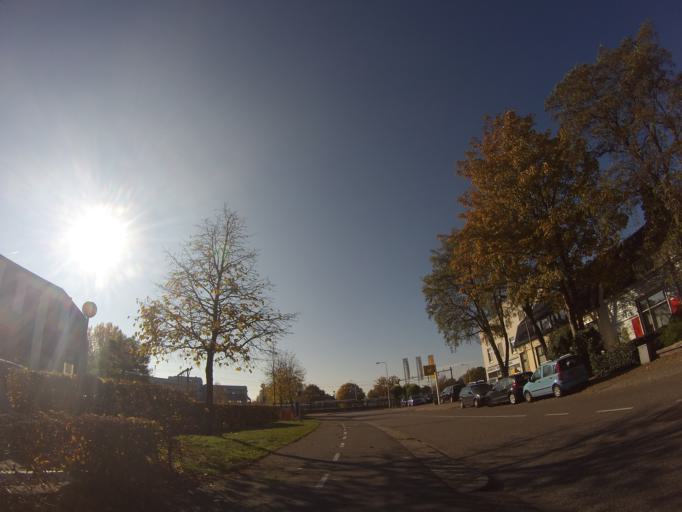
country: NL
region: Utrecht
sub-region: Gemeente Utrechtse Heuvelrug
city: Driebergen-Rijsenburg
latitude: 52.0660
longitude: 5.2580
